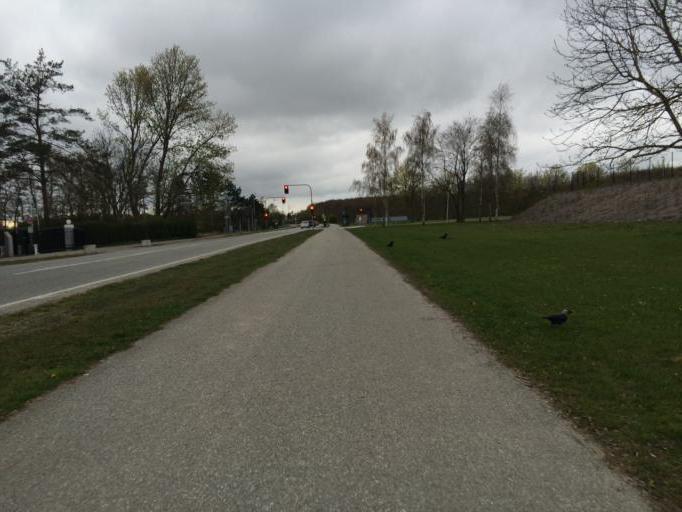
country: DK
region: Capital Region
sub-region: Vallensbaek Kommune
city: Vallensbaek
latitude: 55.6287
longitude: 12.3699
